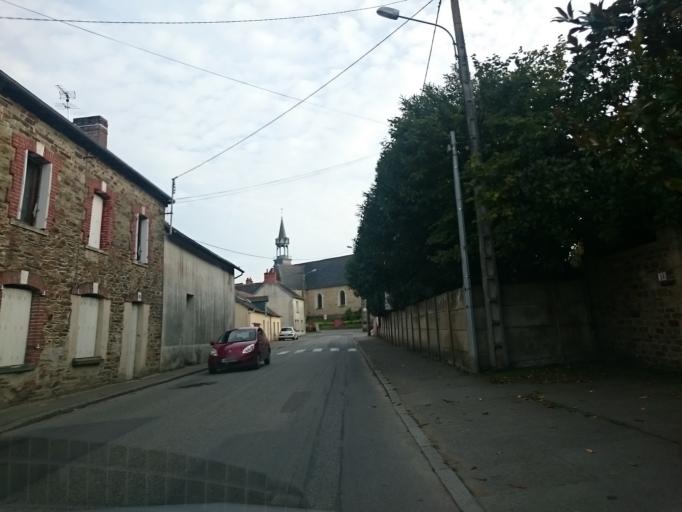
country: FR
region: Brittany
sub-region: Departement d'Ille-et-Vilaine
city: Bourgbarre
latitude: 47.9961
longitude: -1.6158
